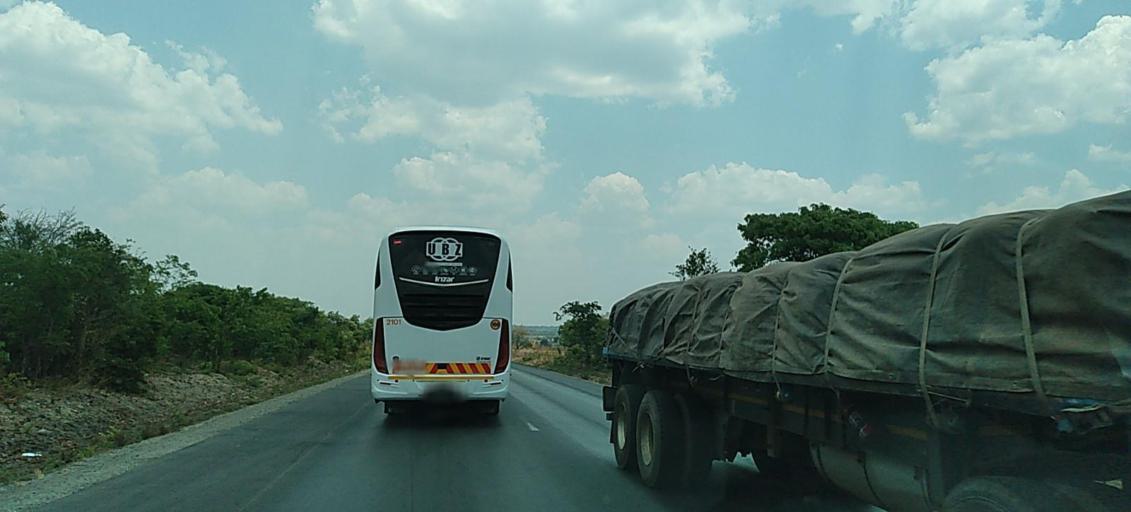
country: ZM
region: Central
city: Kapiri Mposhi
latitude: -14.0682
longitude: 28.6414
